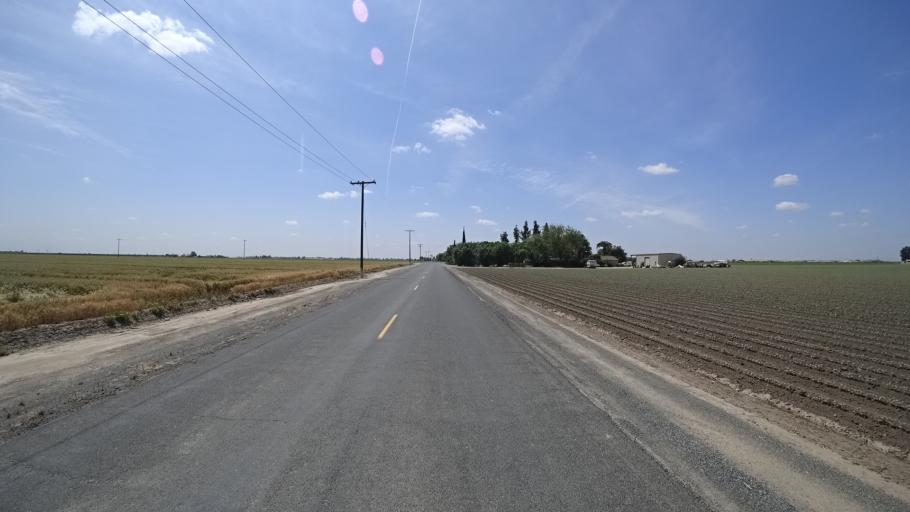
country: US
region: California
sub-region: Tulare County
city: Goshen
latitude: 36.3259
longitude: -119.4752
